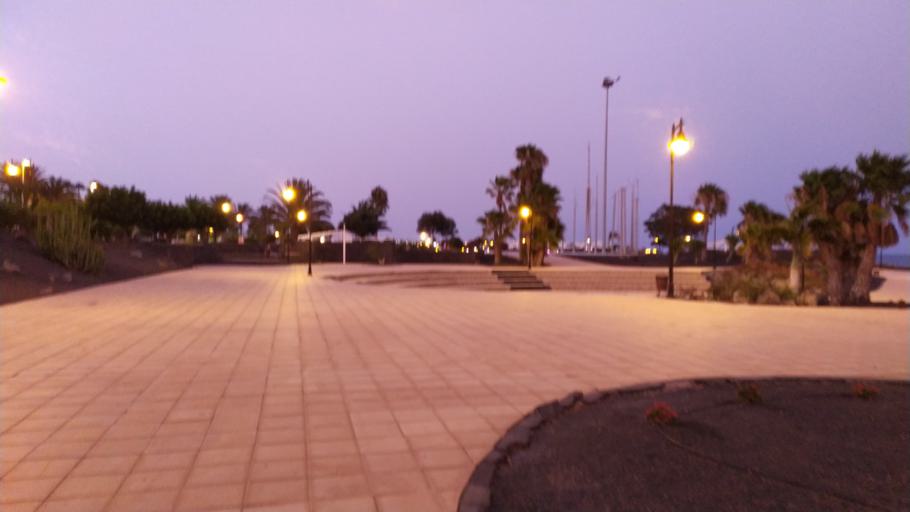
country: ES
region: Canary Islands
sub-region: Provincia de Las Palmas
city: Puerto del Carmen
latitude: 28.9250
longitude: -13.6388
